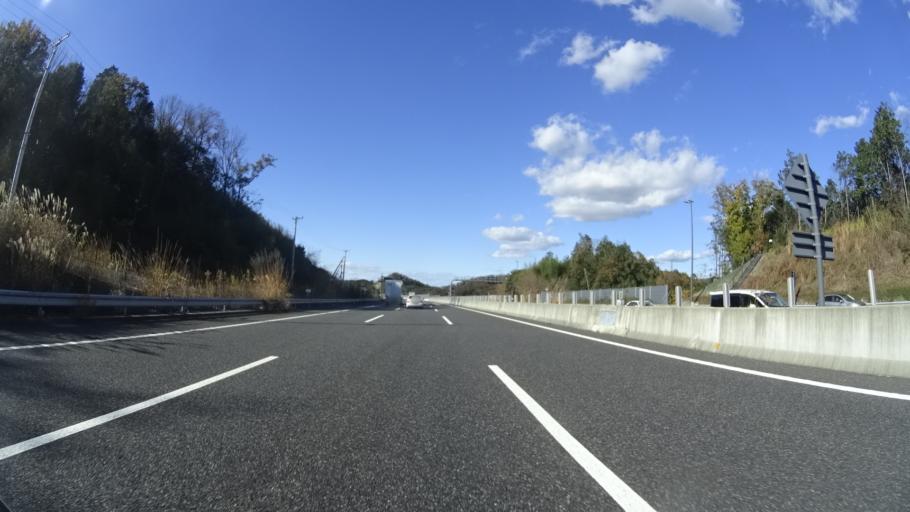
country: JP
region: Aichi
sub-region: Toyota-shi
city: Toyota
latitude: 35.0352
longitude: 137.2178
